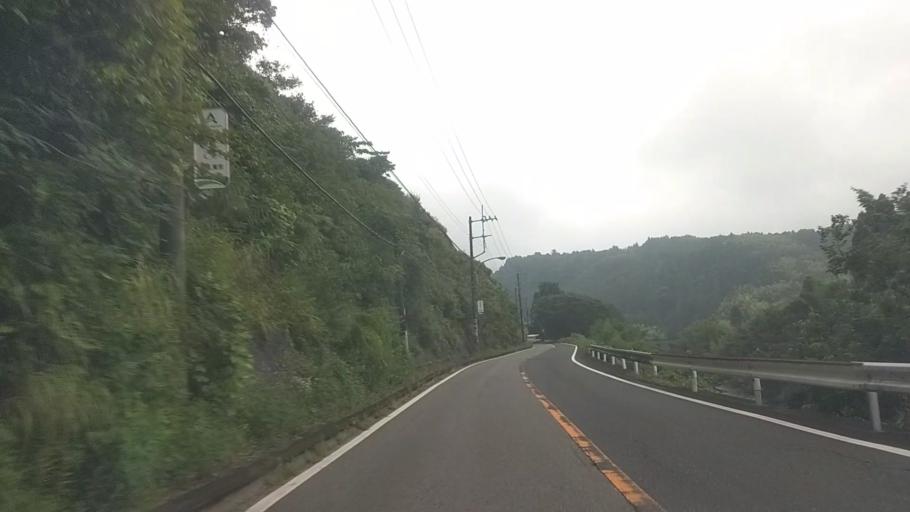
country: JP
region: Chiba
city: Katsuura
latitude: 35.2434
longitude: 140.2379
